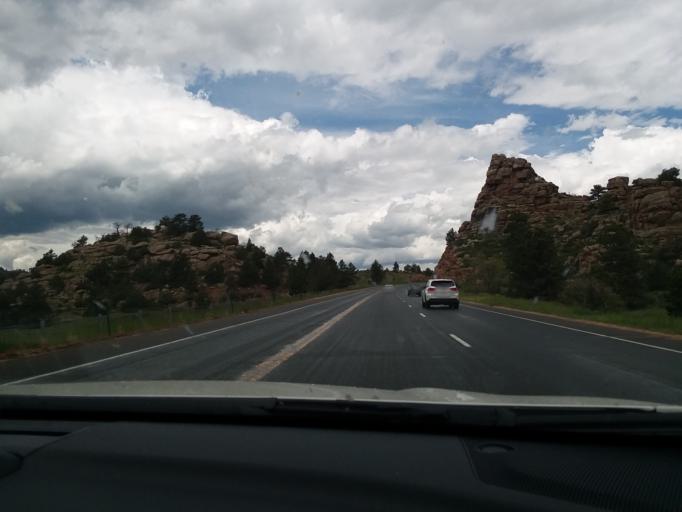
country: US
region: Wyoming
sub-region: Albany County
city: Laramie
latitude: 40.9662
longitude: -105.3762
